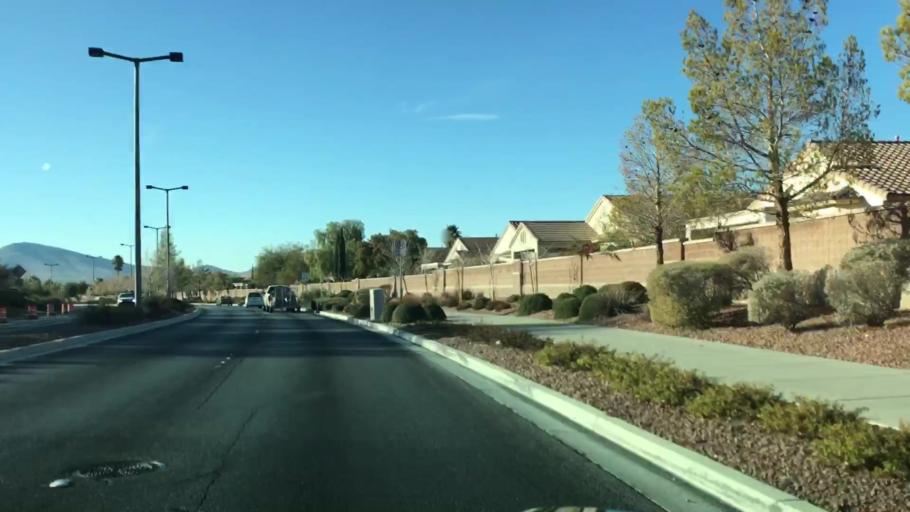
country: US
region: Nevada
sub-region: Clark County
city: Whitney
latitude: 35.9674
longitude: -115.1203
